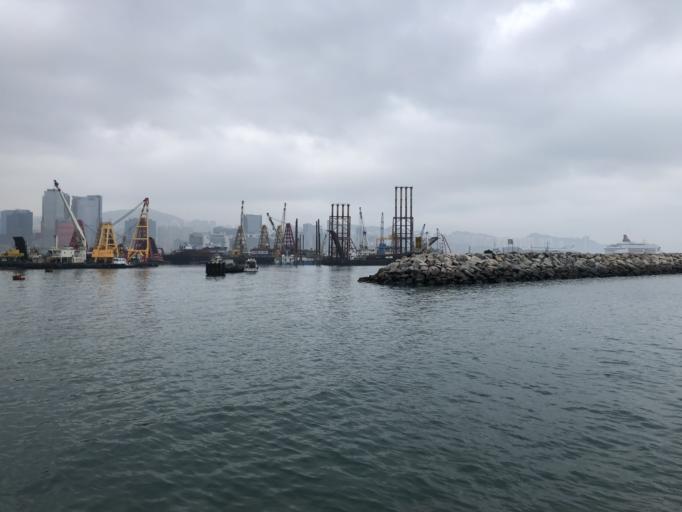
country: HK
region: Kowloon City
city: Kowloon
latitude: 22.3144
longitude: 114.1937
